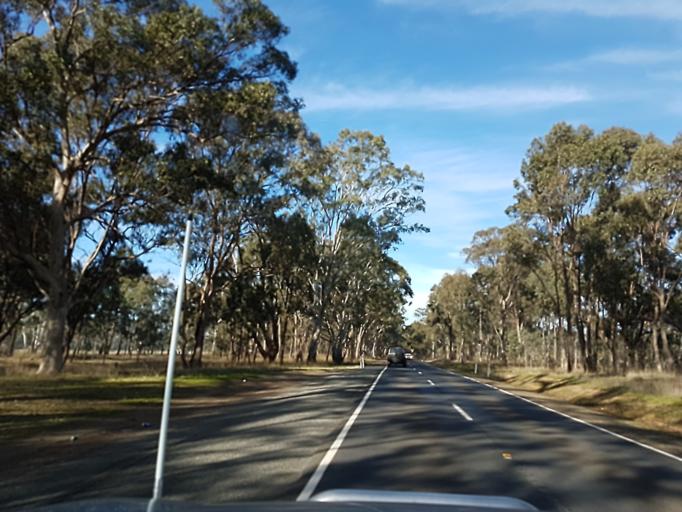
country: AU
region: Victoria
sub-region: Murrindindi
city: Alexandra
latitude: -37.1450
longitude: 145.6350
